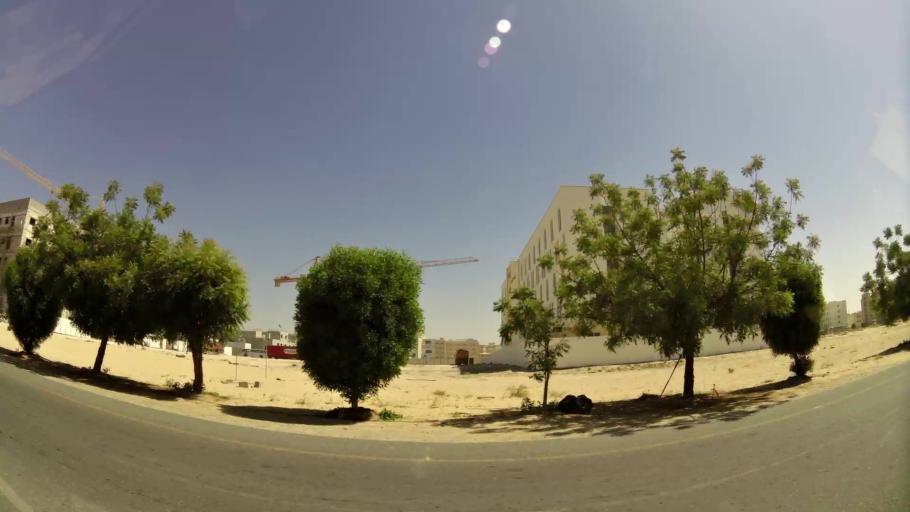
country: AE
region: Dubai
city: Dubai
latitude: 24.9725
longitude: 55.2033
